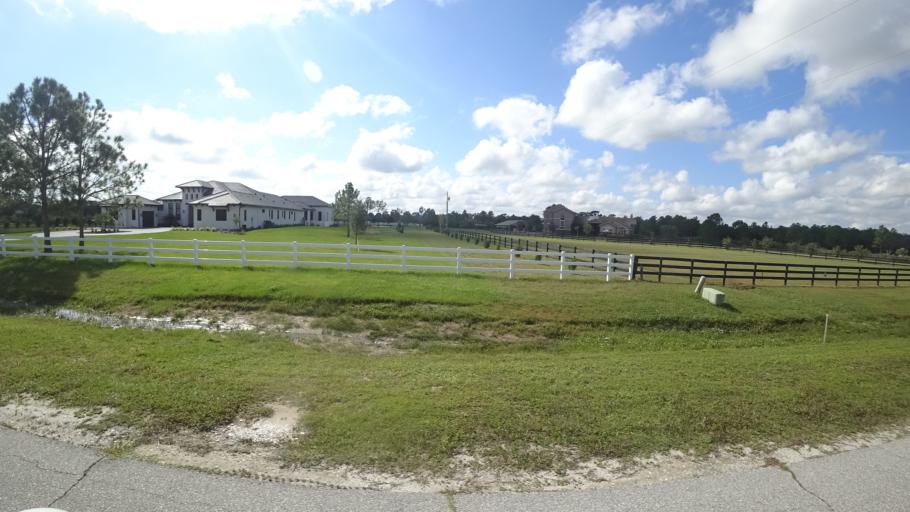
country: US
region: Florida
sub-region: Sarasota County
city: The Meadows
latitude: 27.4024
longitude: -82.3336
